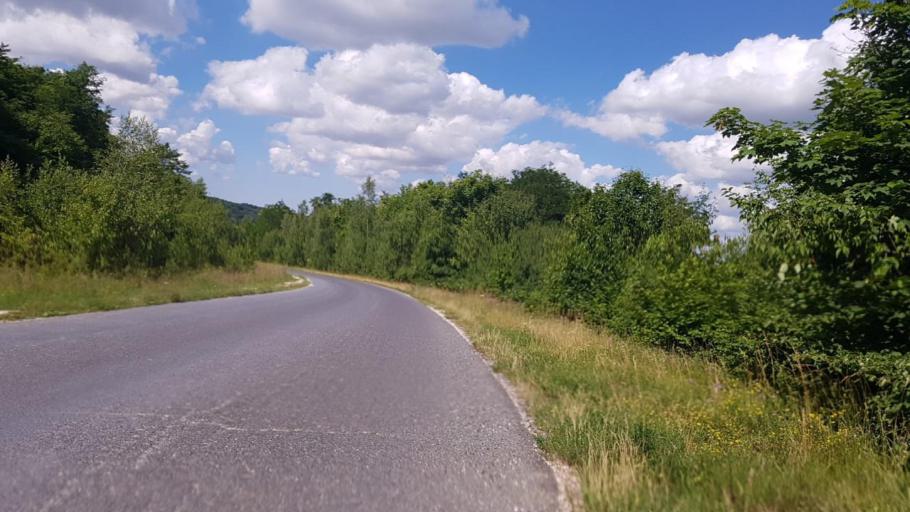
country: FR
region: Lorraine
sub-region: Departement de la Meuse
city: Vacon
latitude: 48.6886
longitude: 5.6689
